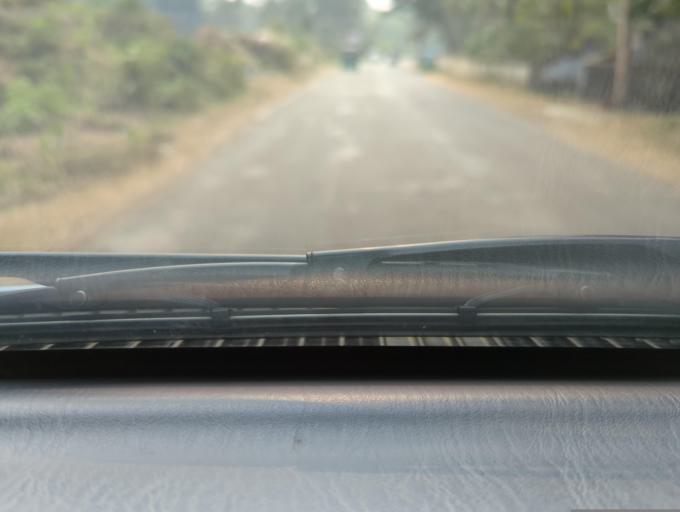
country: BD
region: Sylhet
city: Maulavi Bazar
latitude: 24.5282
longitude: 91.7340
